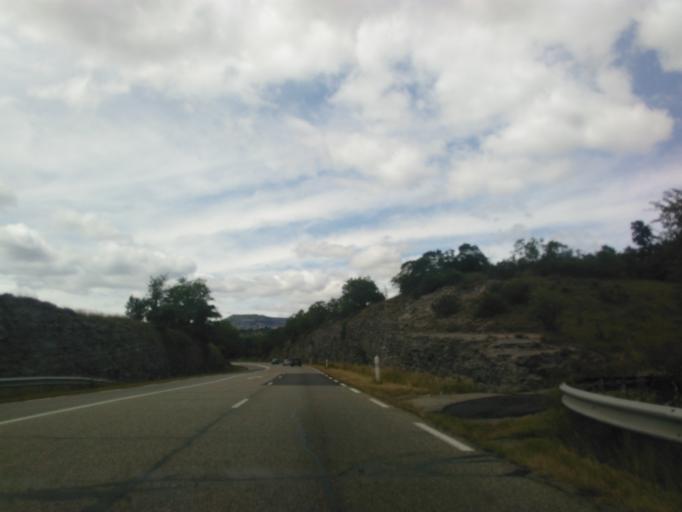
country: FR
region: Rhone-Alpes
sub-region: Departement de l'Ardeche
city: Alba-la-Romaine
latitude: 44.5789
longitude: 4.5768
